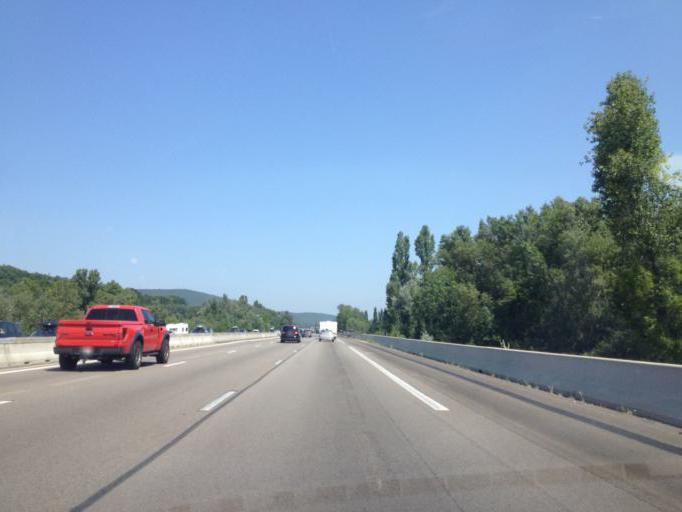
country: FR
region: Rhone-Alpes
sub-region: Departement de la Drome
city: Saint-Marcel-les-Sauzet
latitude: 44.5823
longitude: 4.8045
